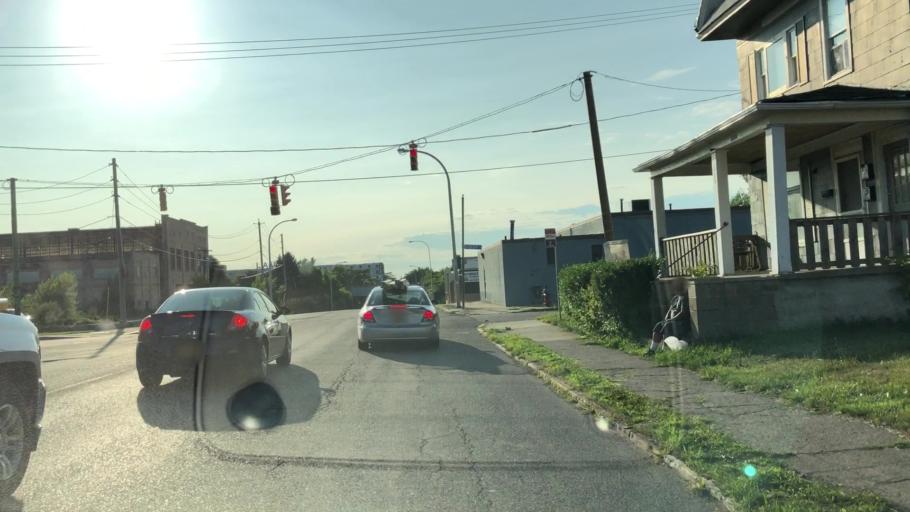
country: US
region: New York
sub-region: Erie County
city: West Seneca
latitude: 42.8760
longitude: -78.8301
